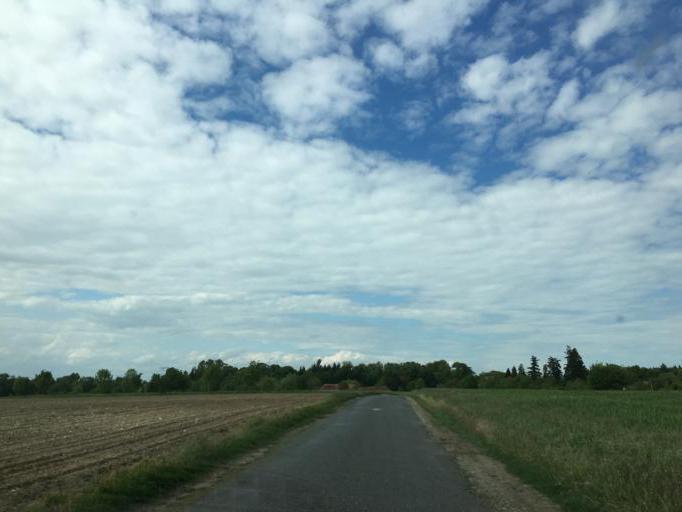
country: FR
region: Centre
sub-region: Departement du Loiret
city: Dry
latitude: 47.7825
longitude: 1.7011
